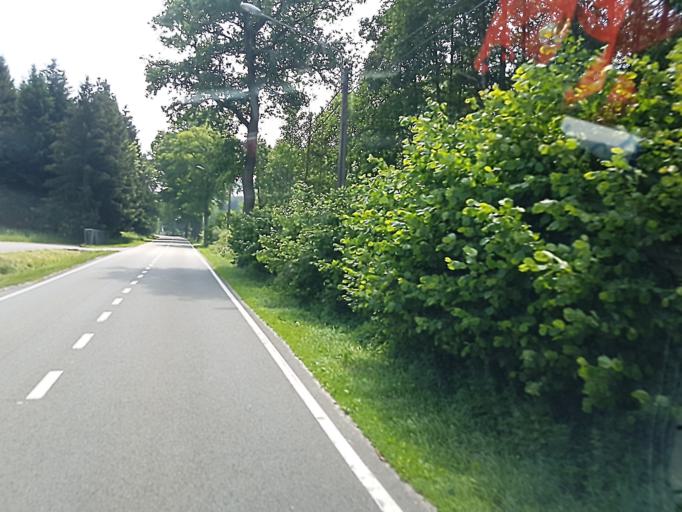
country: BE
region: Wallonia
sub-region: Province de Liege
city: Trois-Ponts
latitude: 50.3604
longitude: 5.8383
